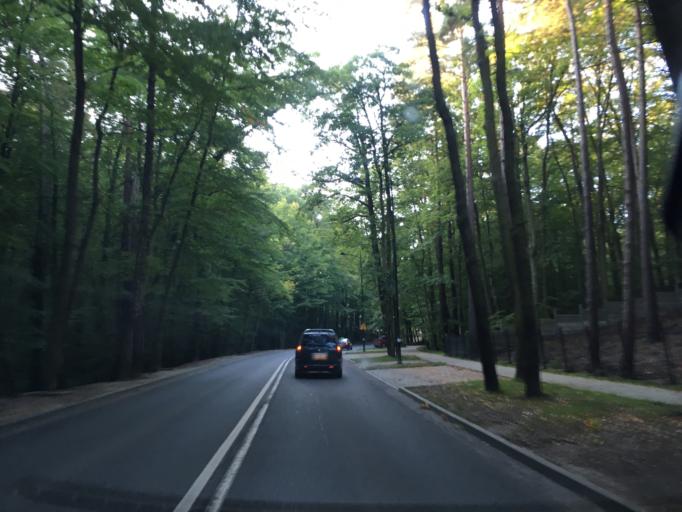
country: PL
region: Pomeranian Voivodeship
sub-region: Sopot
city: Sopot
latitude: 54.4517
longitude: 18.5431
